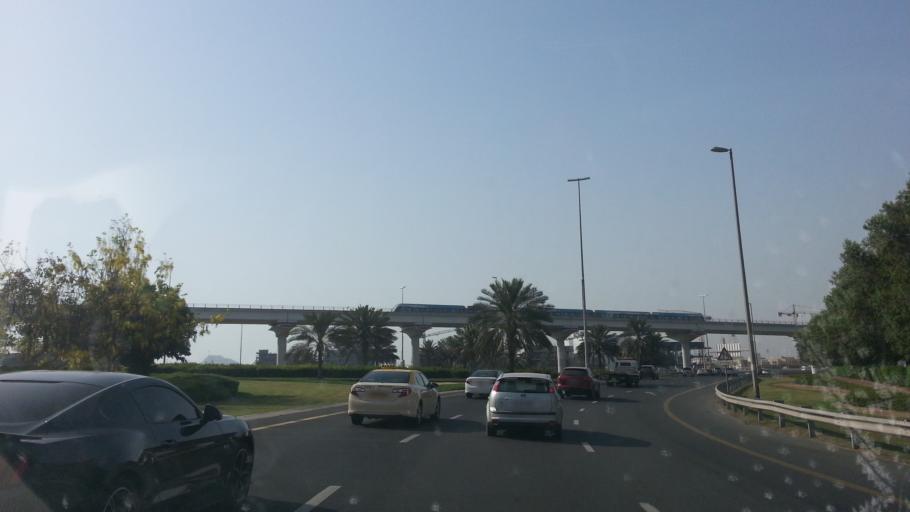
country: AE
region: Dubai
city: Dubai
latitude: 25.1218
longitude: 55.2041
